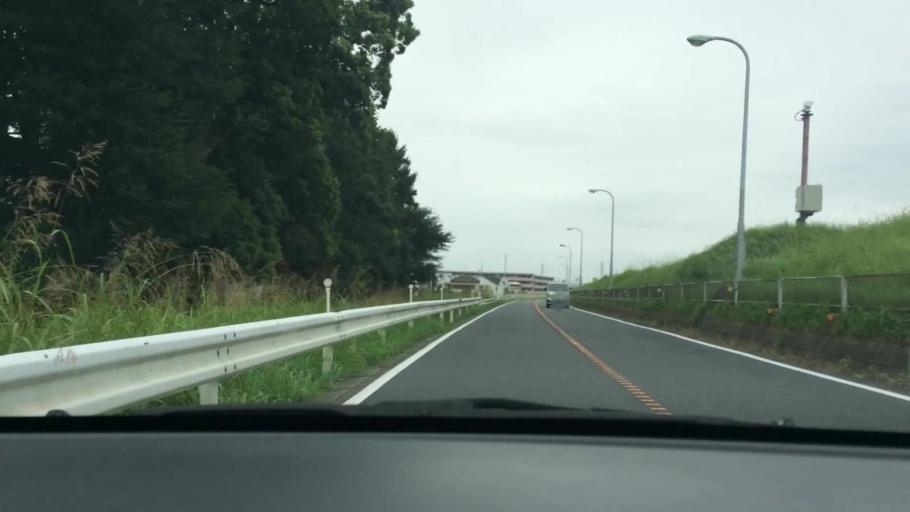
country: JP
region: Chiba
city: Matsudo
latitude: 35.7705
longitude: 139.8786
